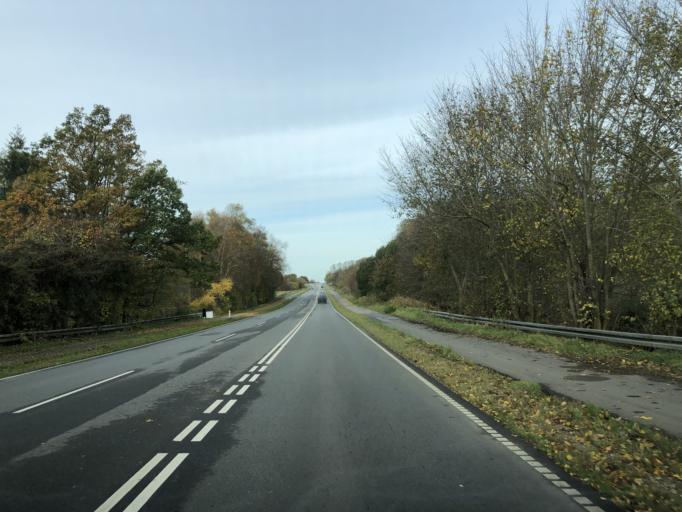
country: DK
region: Capital Region
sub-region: Rudersdal Kommune
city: Birkerod
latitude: 55.8538
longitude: 12.4143
